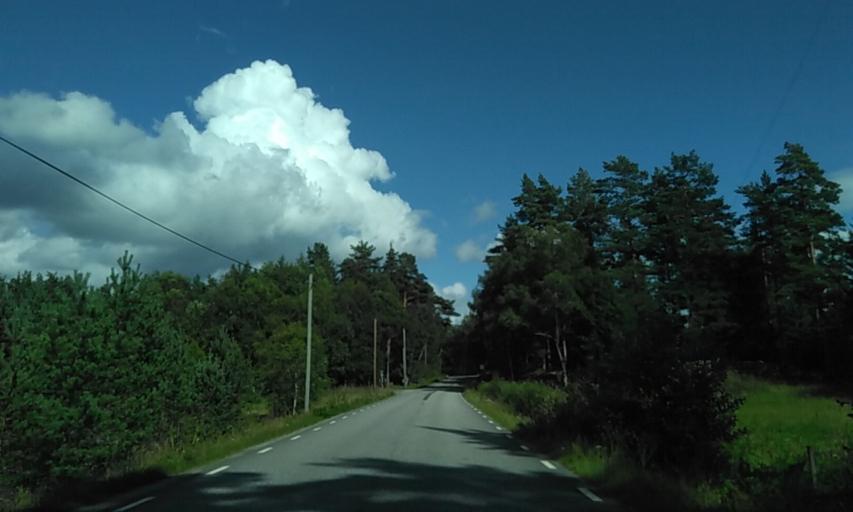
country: SE
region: Vaestra Goetaland
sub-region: Vargarda Kommun
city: Jonstorp
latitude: 57.9427
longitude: 12.7861
